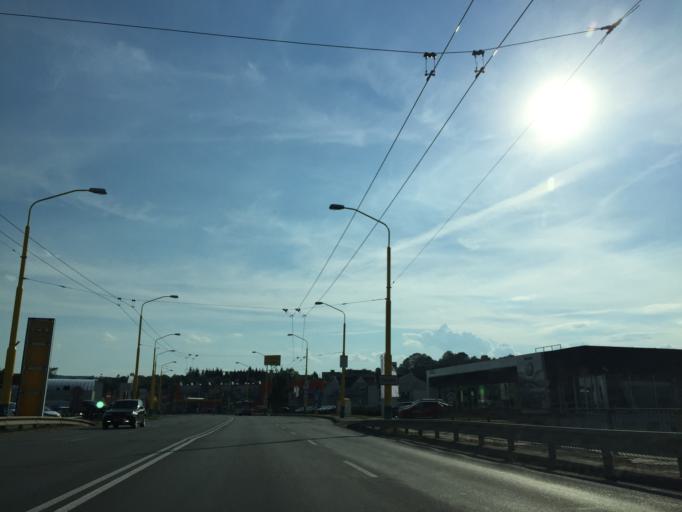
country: SK
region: Presovsky
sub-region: Okres Presov
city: Presov
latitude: 49.0088
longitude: 21.2513
